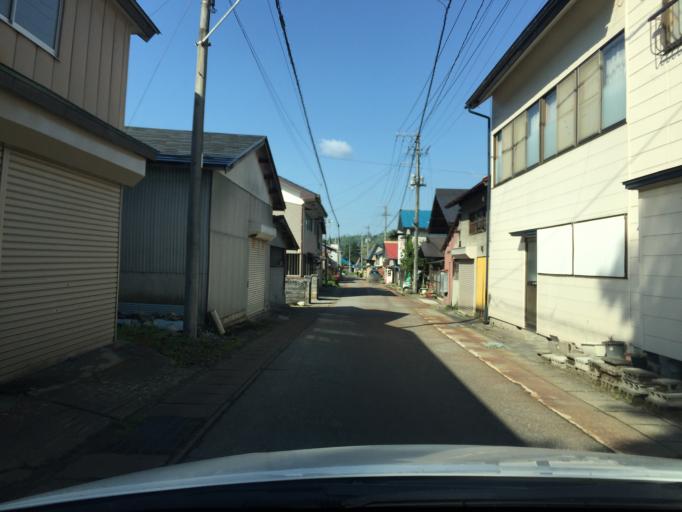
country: JP
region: Fukushima
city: Kitakata
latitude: 37.6779
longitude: 139.6523
